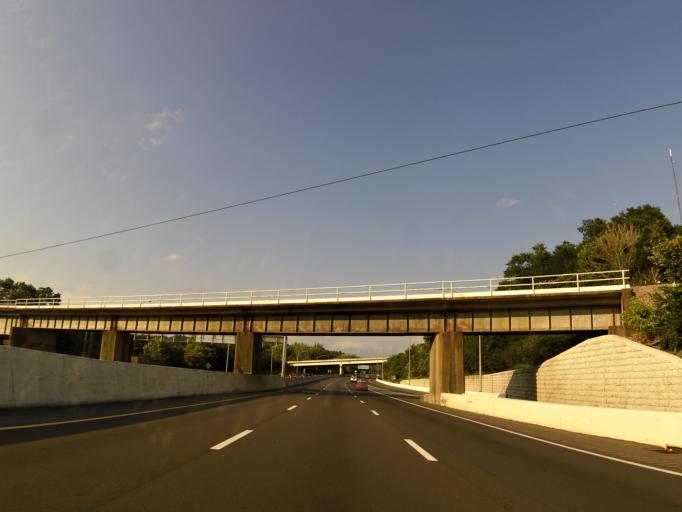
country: US
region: Tennessee
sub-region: Knox County
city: Knoxville
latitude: 36.0018
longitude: -83.9565
